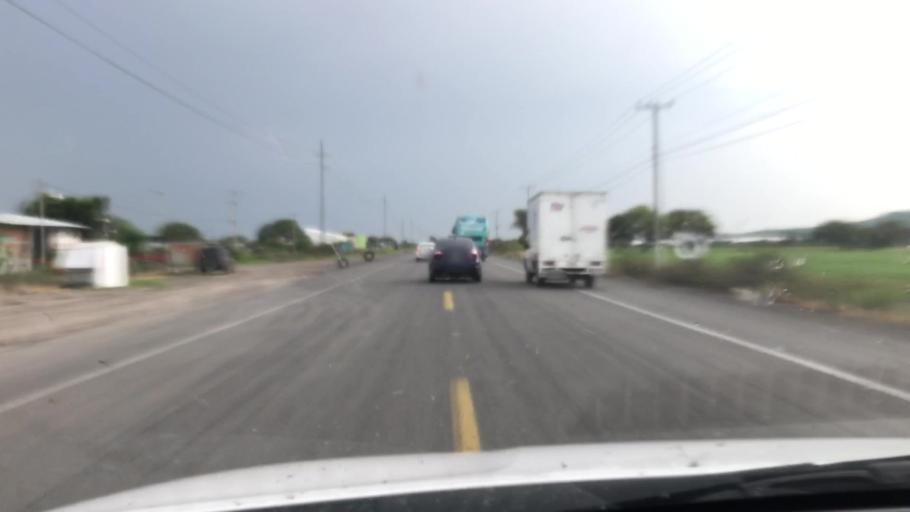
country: MX
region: Michoacan
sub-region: Vista Hermosa
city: Los Pilares
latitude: 20.2767
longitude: -102.3872
